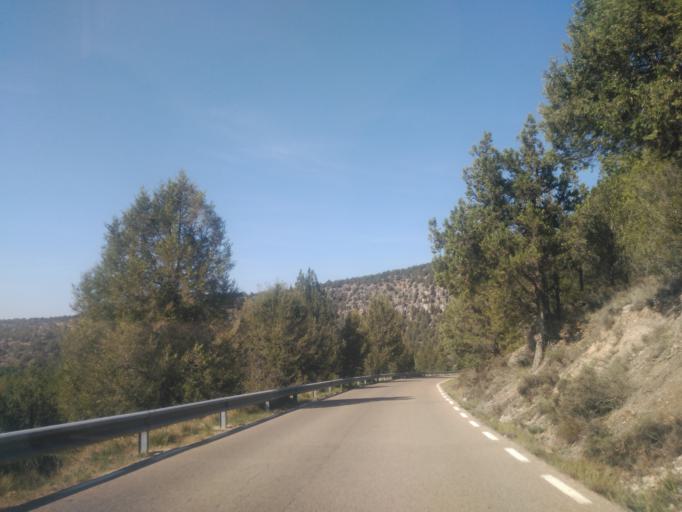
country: ES
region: Castille and Leon
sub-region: Provincia de Soria
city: Ucero
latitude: 41.7271
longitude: -3.0415
